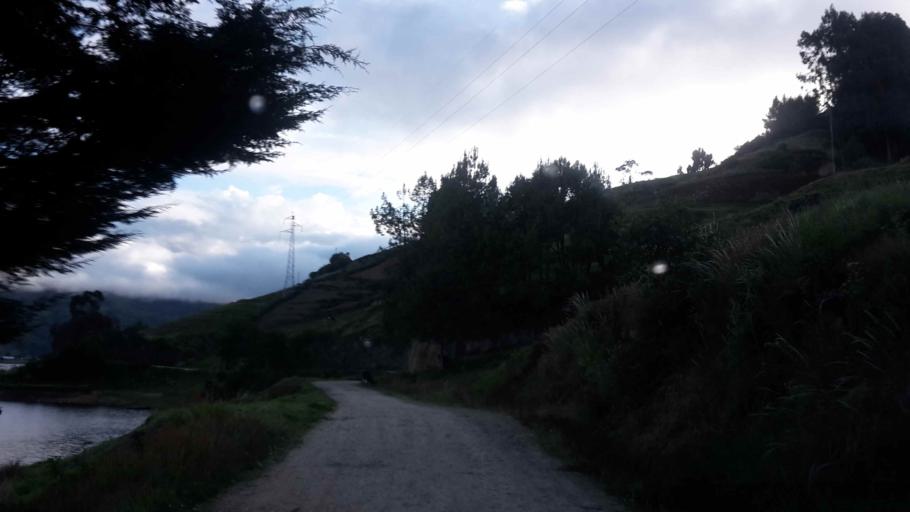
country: BO
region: Cochabamba
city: Colomi
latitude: -17.2716
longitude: -65.9063
